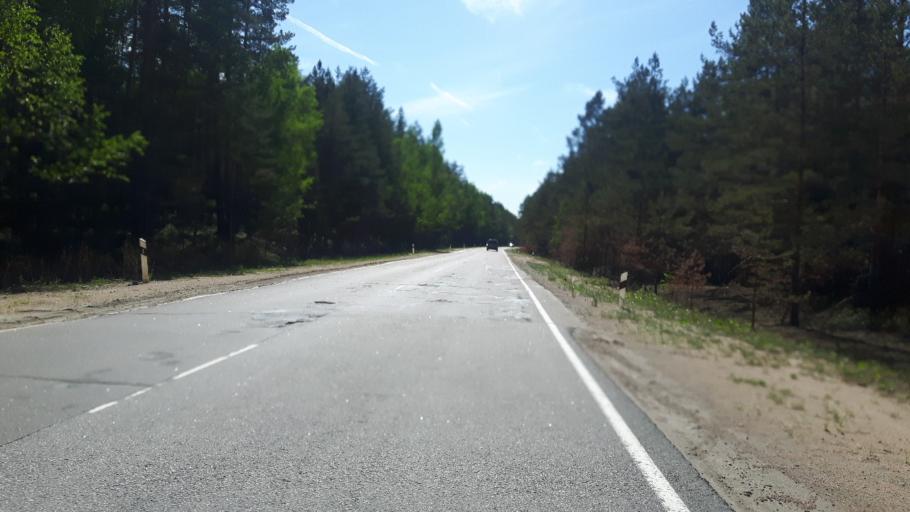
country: RU
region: Leningrad
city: Sista-Palkino
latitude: 59.7763
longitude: 28.8606
